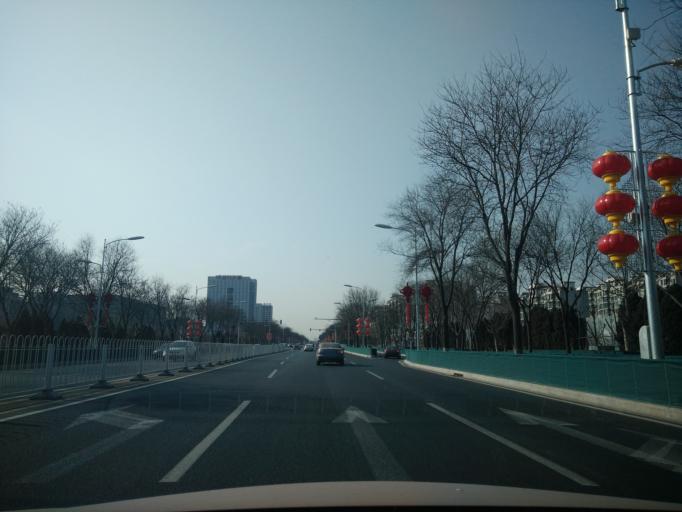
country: CN
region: Beijing
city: Jiugong
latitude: 39.7884
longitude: 116.4971
